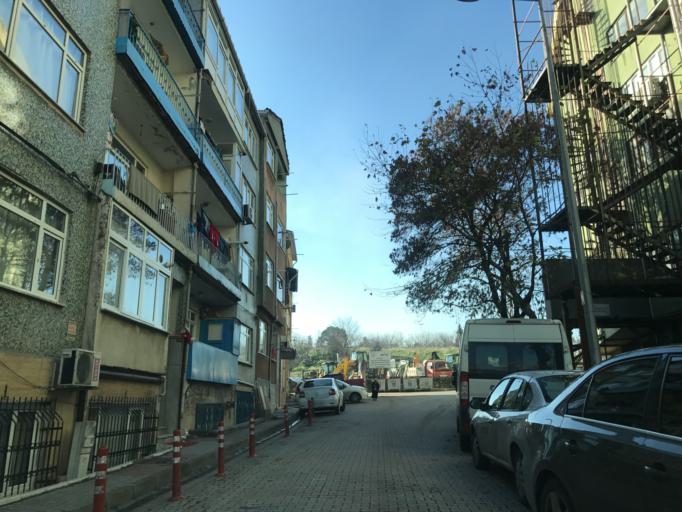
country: TR
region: Istanbul
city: Istanbul
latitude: 41.0374
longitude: 28.9337
